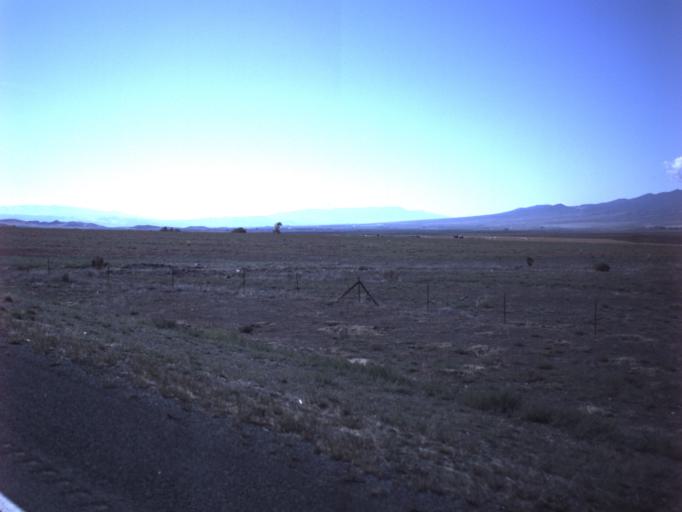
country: US
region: Utah
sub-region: Sanpete County
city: Gunnison
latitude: 39.2508
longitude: -111.8580
